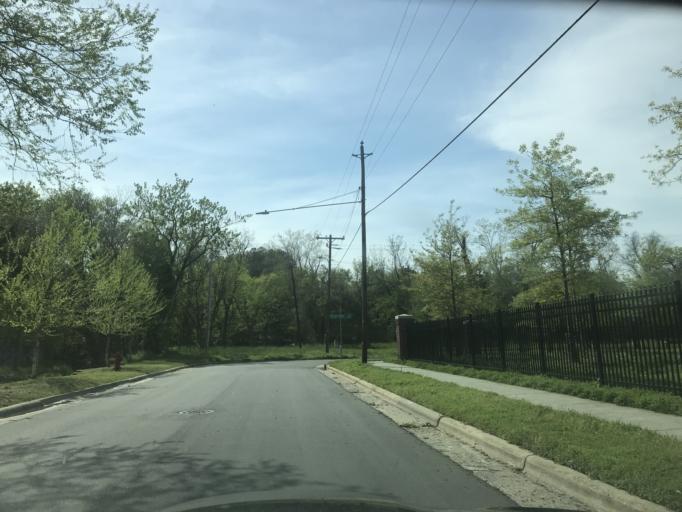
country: US
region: North Carolina
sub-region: Wake County
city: Raleigh
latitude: 35.7636
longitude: -78.6418
